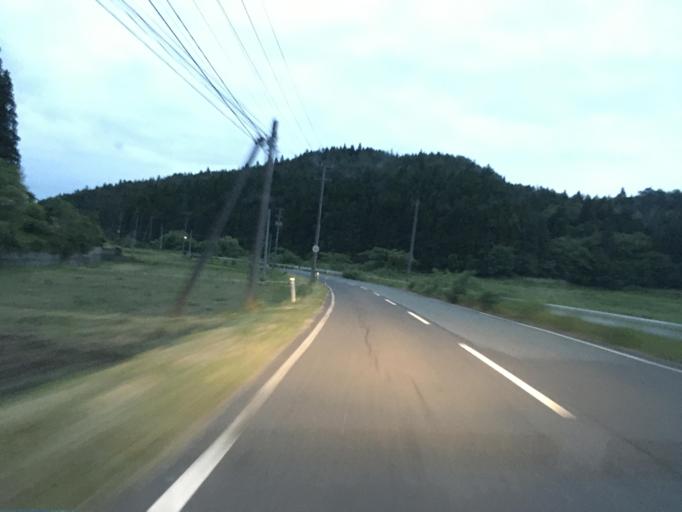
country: JP
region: Miyagi
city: Furukawa
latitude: 38.7646
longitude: 140.8749
